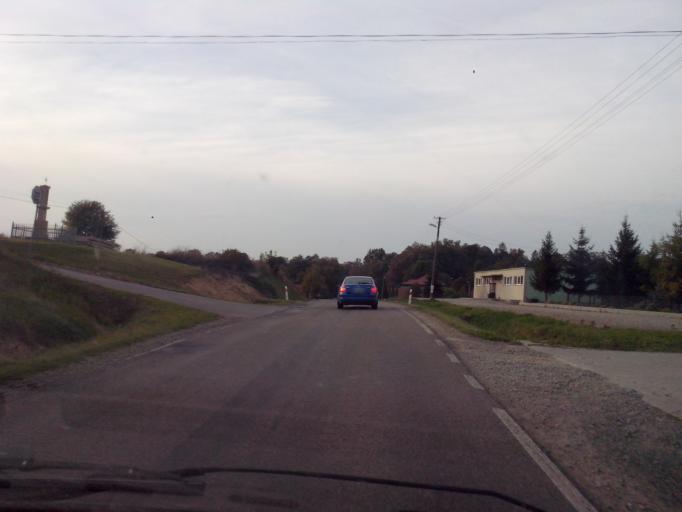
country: PL
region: Subcarpathian Voivodeship
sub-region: Powiat strzyzowski
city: Jawornik
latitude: 49.8140
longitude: 21.8427
